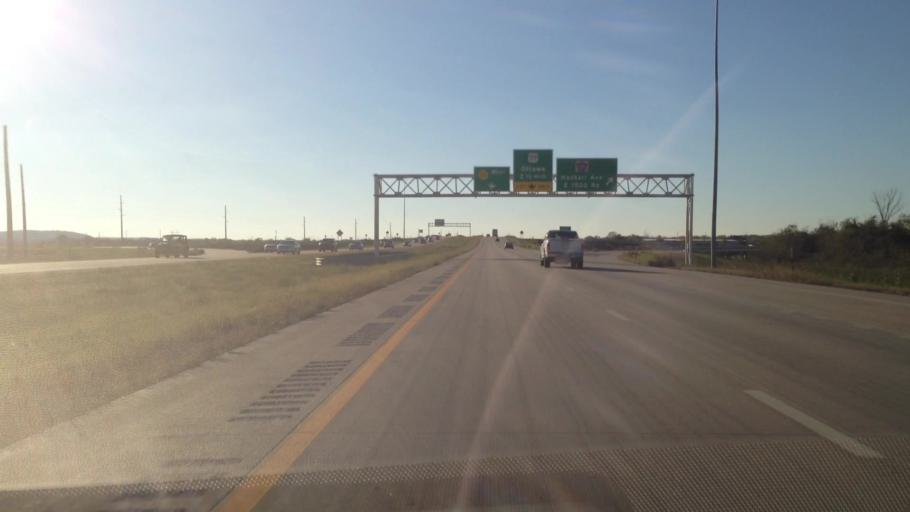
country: US
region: Kansas
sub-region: Douglas County
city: Lawrence
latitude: 38.9242
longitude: -95.2127
